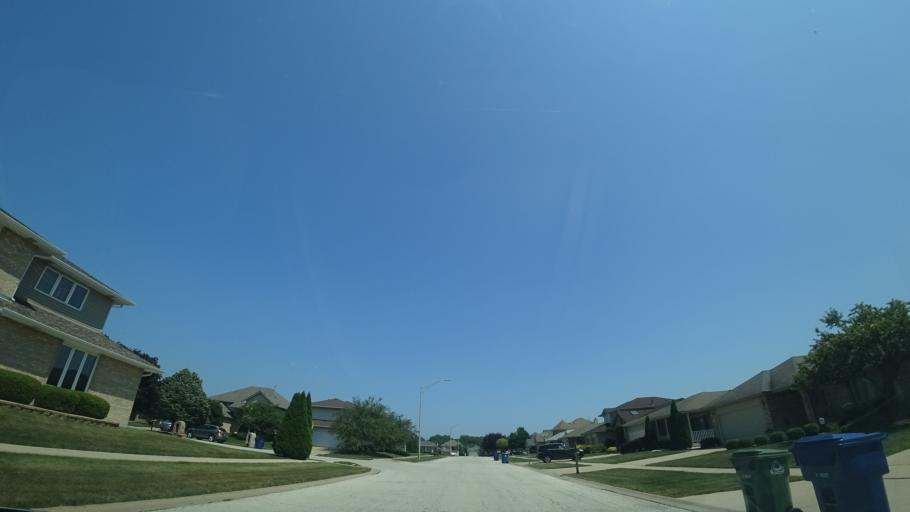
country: US
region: Illinois
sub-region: Cook County
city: Oak Lawn
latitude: 41.6938
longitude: -87.7542
